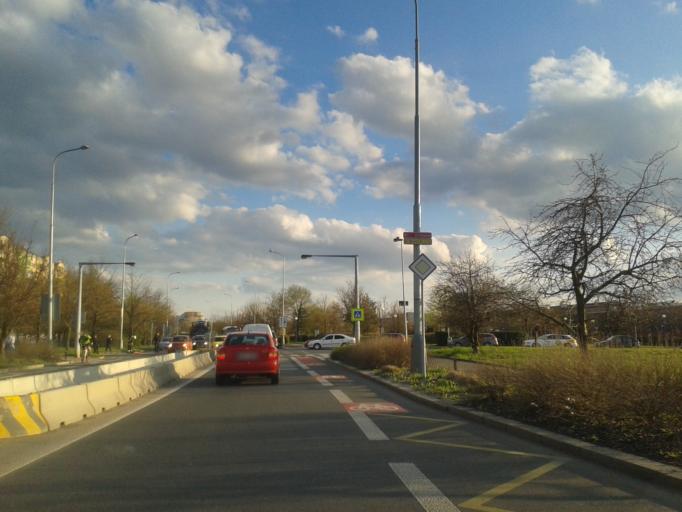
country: CZ
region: Praha
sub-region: Praha 18
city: Letnany
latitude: 50.1389
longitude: 14.5047
